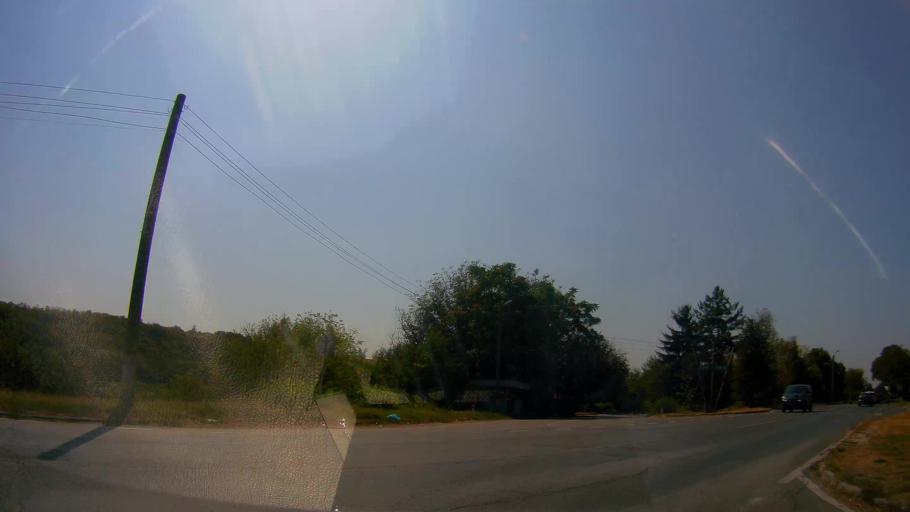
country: BG
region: Ruse
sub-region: Obshtina Vetovo
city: Senovo
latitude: 43.5614
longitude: 26.4046
